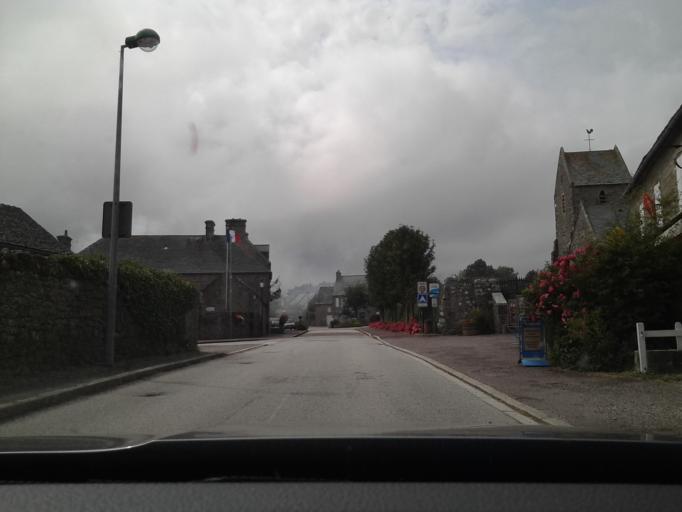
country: FR
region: Lower Normandy
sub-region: Departement de la Manche
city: Beaumont-Hague
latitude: 49.6747
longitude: -1.7996
